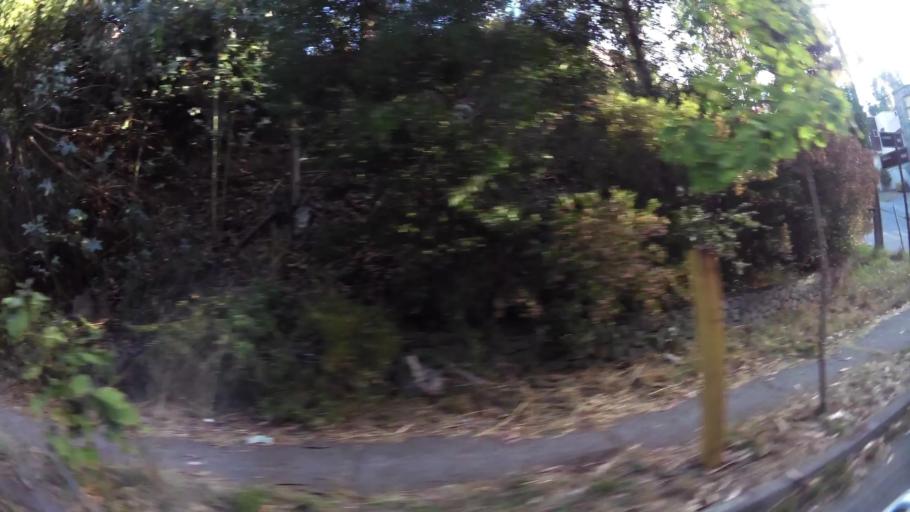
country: CL
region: Biobio
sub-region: Provincia de Concepcion
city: Concepcion
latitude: -36.8588
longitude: -73.0969
